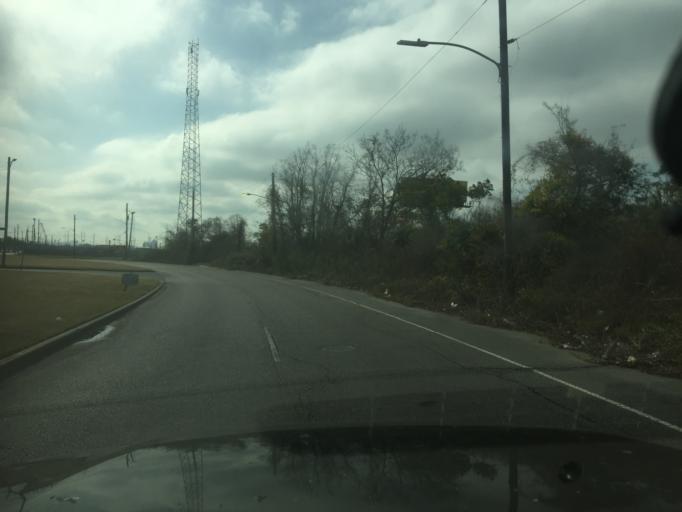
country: US
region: Louisiana
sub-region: Orleans Parish
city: New Orleans
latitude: 29.9989
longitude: -90.0415
